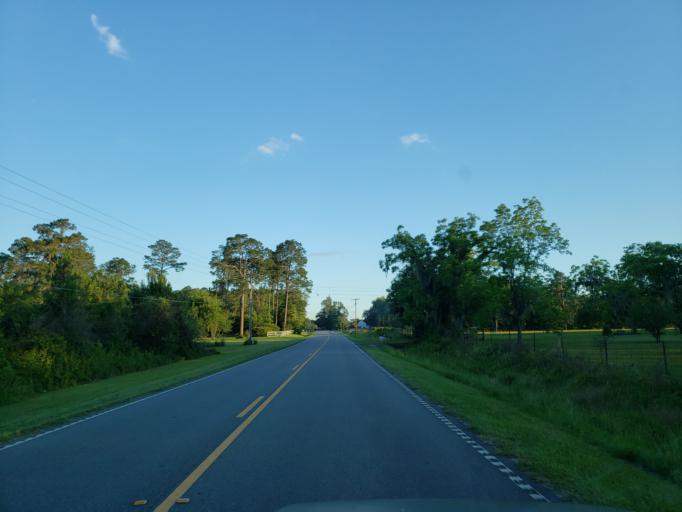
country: US
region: Georgia
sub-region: Lowndes County
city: Valdosta
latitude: 30.7415
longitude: -83.2517
